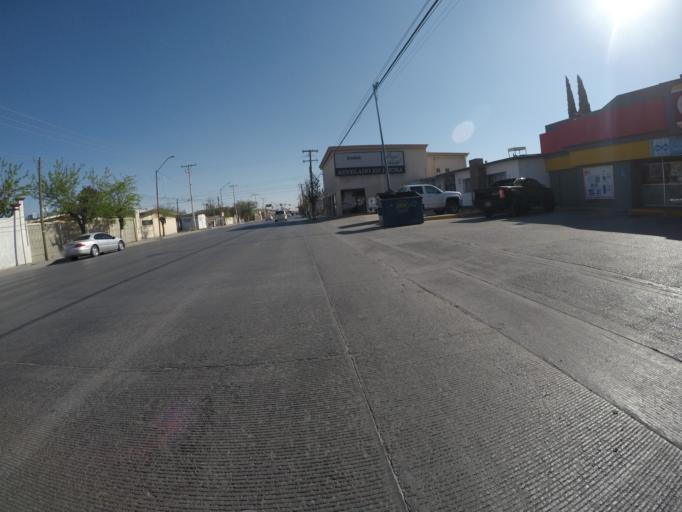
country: MX
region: Chihuahua
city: Ciudad Juarez
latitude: 31.7280
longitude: -106.4504
